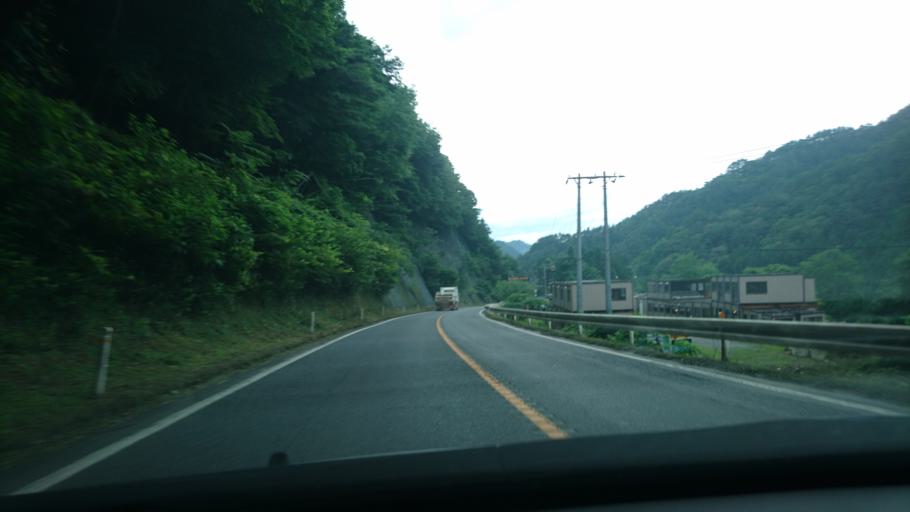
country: JP
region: Iwate
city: Kamaishi
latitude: 39.2940
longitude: 141.8826
